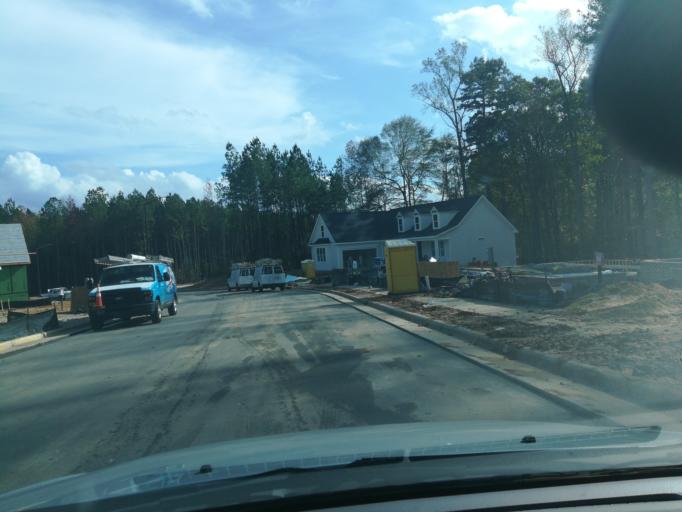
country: US
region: North Carolina
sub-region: Durham County
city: Durham
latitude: 36.0575
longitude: -78.9417
